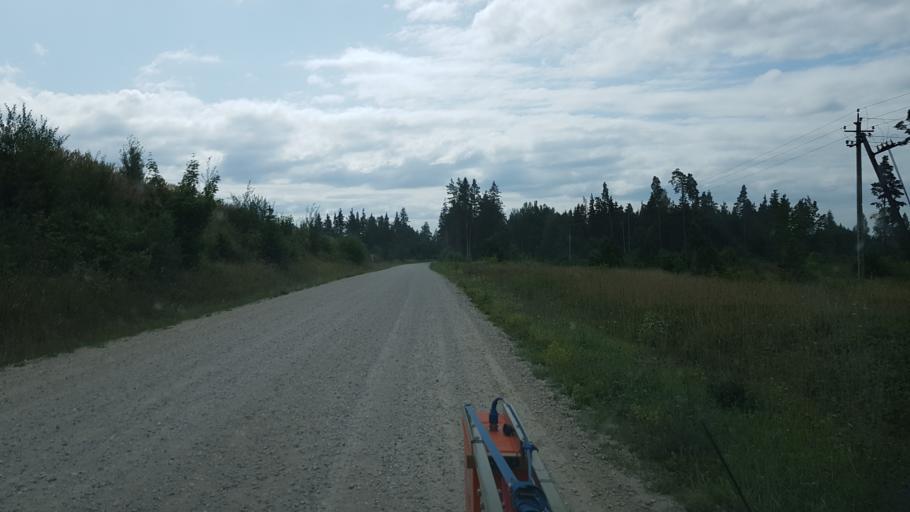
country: EE
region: Paernumaa
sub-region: Halinga vald
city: Parnu-Jaagupi
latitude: 58.5737
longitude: 24.4080
